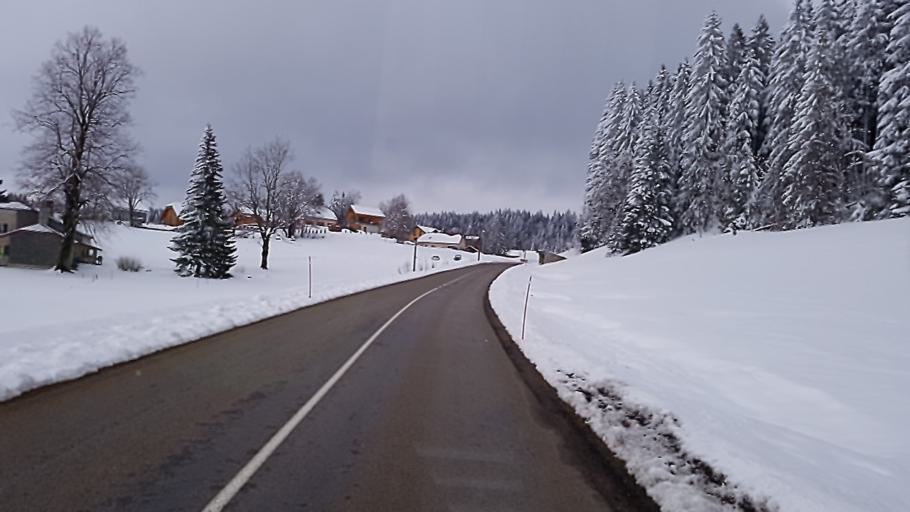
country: FR
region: Franche-Comte
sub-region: Departement du Jura
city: Longchaumois
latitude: 46.3964
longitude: 5.9601
